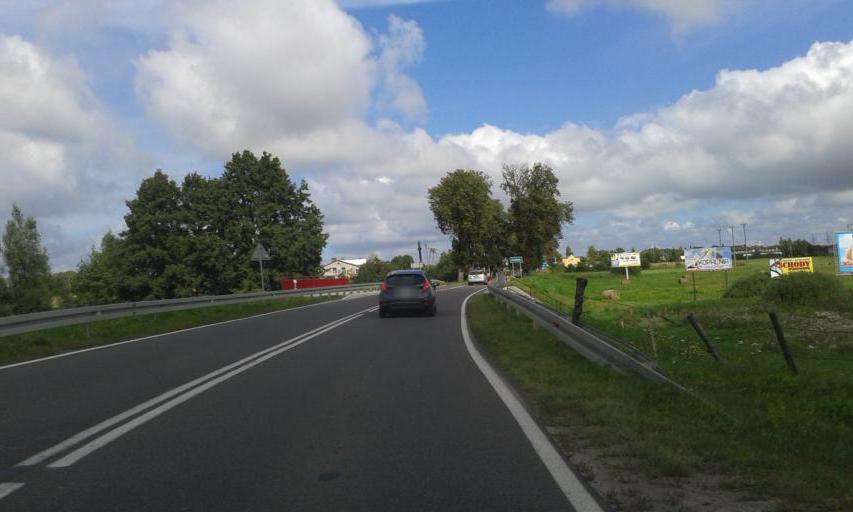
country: PL
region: West Pomeranian Voivodeship
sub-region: Powiat slawienski
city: Darlowo
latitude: 54.4050
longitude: 16.4106
